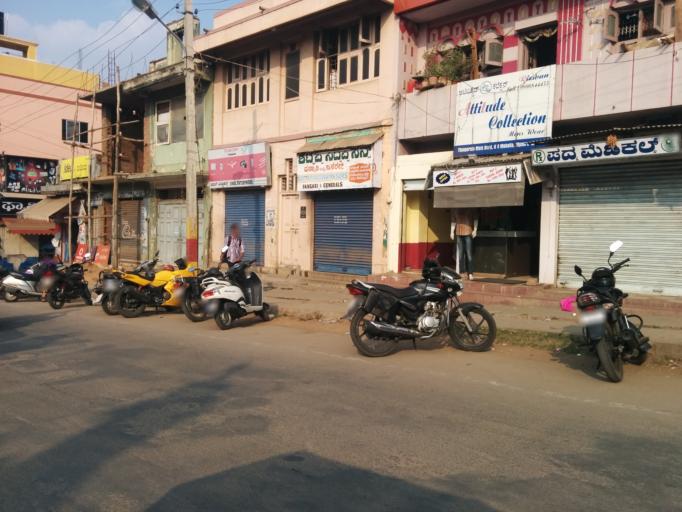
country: IN
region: Karnataka
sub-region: Mysore
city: Mysore
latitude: 12.2967
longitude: 76.6518
